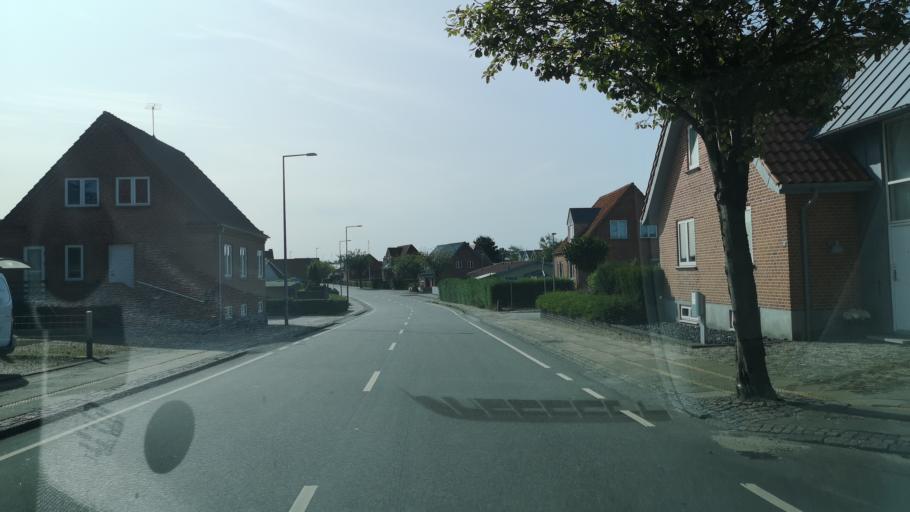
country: DK
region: Central Jutland
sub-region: Ringkobing-Skjern Kommune
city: Videbaek
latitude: 56.0889
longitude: 8.6302
